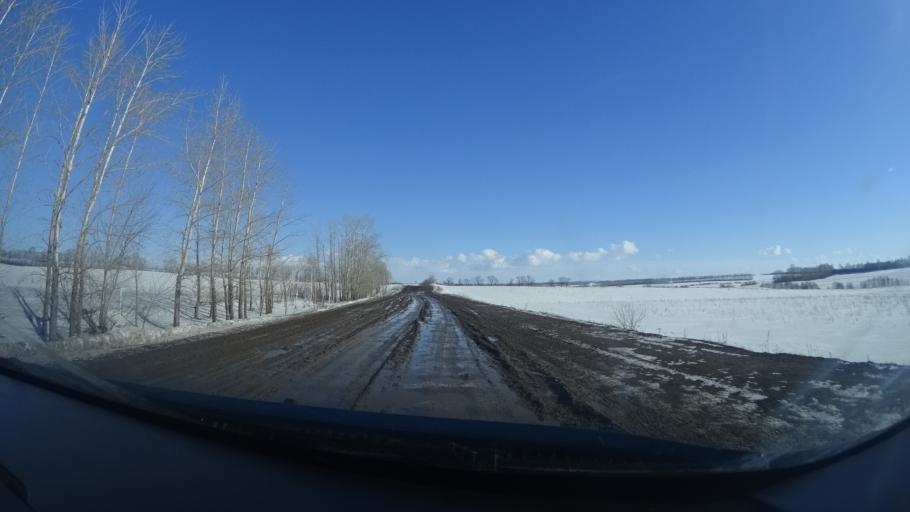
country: RU
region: Bashkortostan
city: Chishmy
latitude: 54.6005
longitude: 55.2281
